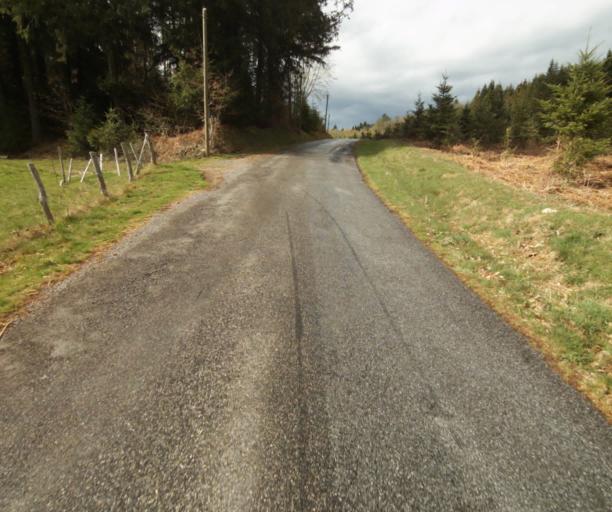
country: FR
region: Limousin
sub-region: Departement de la Correze
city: Saint-Privat
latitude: 45.2512
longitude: 1.9893
